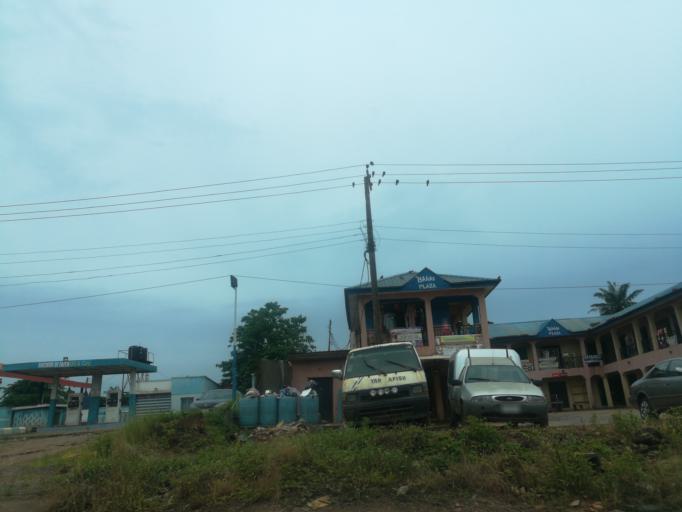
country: NG
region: Oyo
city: Ibadan
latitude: 7.3913
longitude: 3.9620
